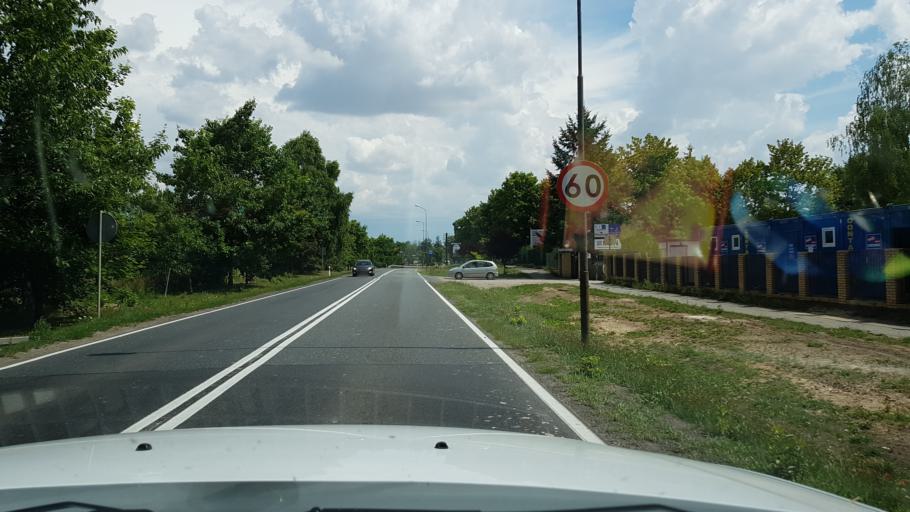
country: PL
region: West Pomeranian Voivodeship
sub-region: Powiat walecki
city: Walcz
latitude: 53.2837
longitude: 16.4491
